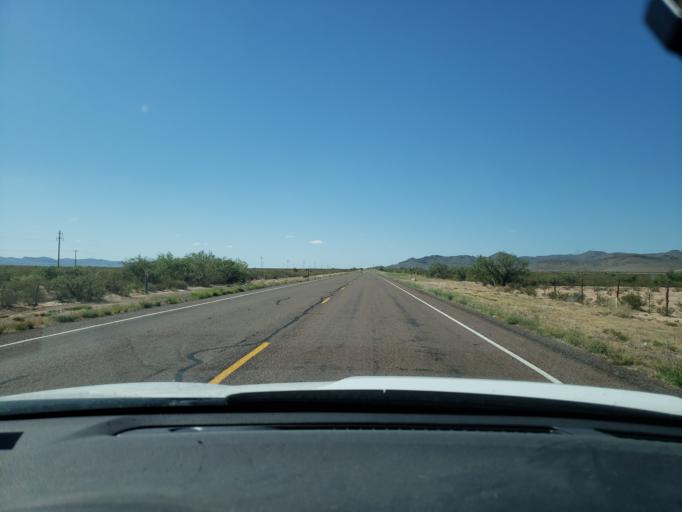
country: US
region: Texas
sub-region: Culberson County
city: Van Horn
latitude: 30.9434
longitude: -104.8118
